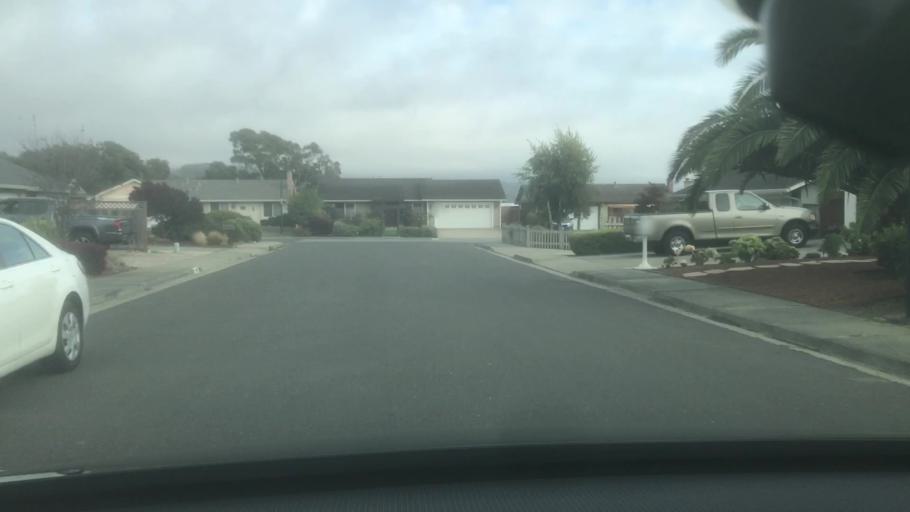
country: US
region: California
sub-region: San Mateo County
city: Half Moon Bay
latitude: 37.4814
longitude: -122.4396
